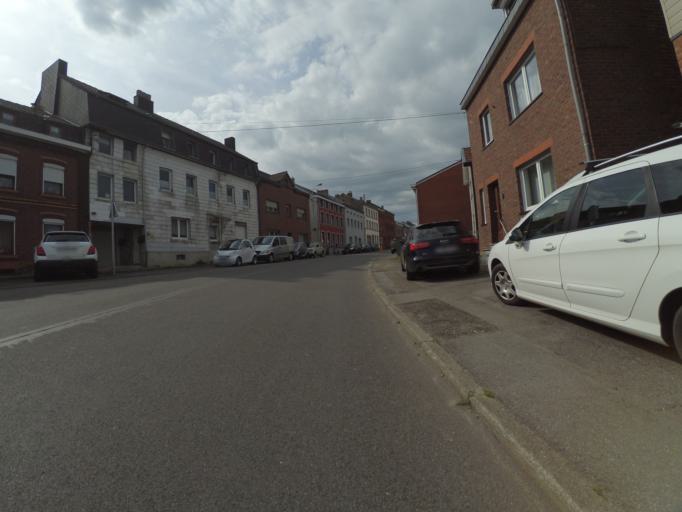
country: BE
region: Wallonia
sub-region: Province de Liege
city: La Calamine
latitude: 50.7207
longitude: 6.0102
